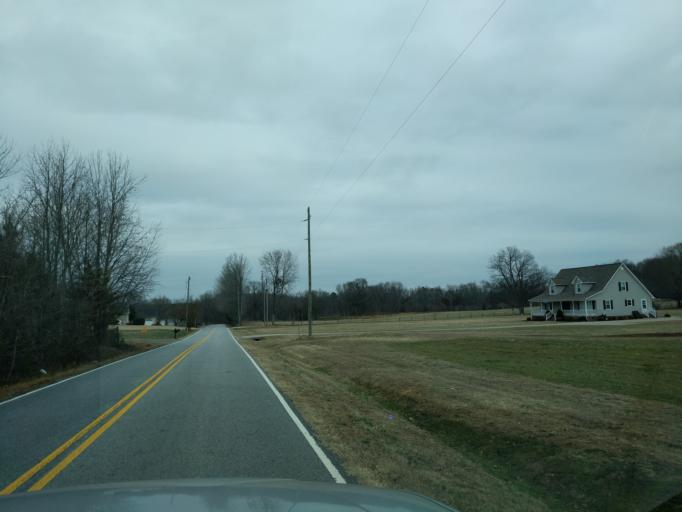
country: US
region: South Carolina
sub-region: Spartanburg County
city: Duncan
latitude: 34.8653
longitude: -82.1265
